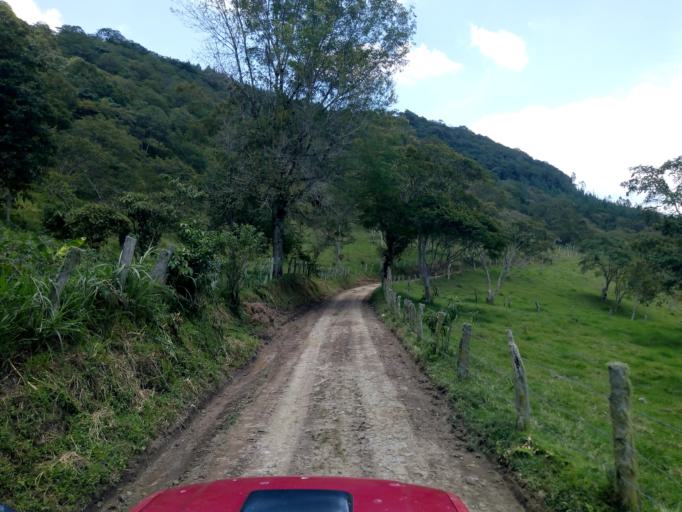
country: CO
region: Boyaca
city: Moniquira
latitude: 5.8663
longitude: -73.5155
